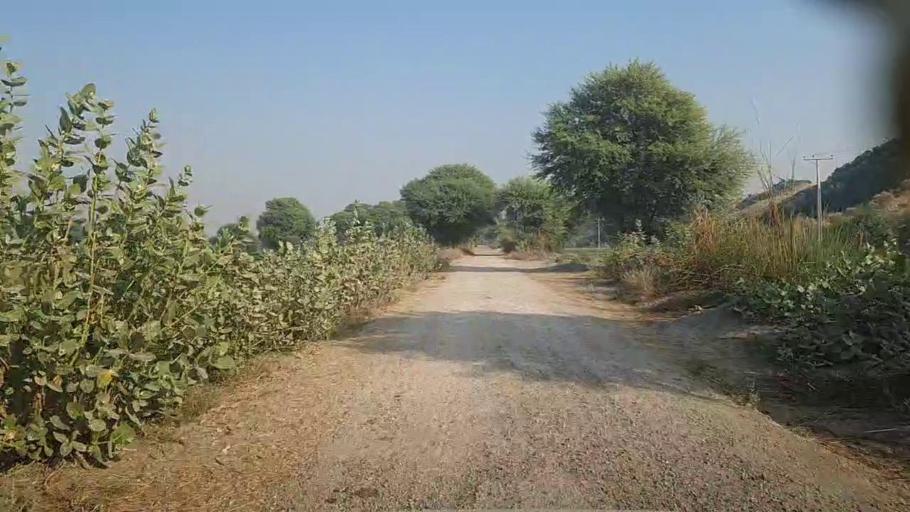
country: PK
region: Sindh
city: Karaundi
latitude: 26.7661
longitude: 68.4766
